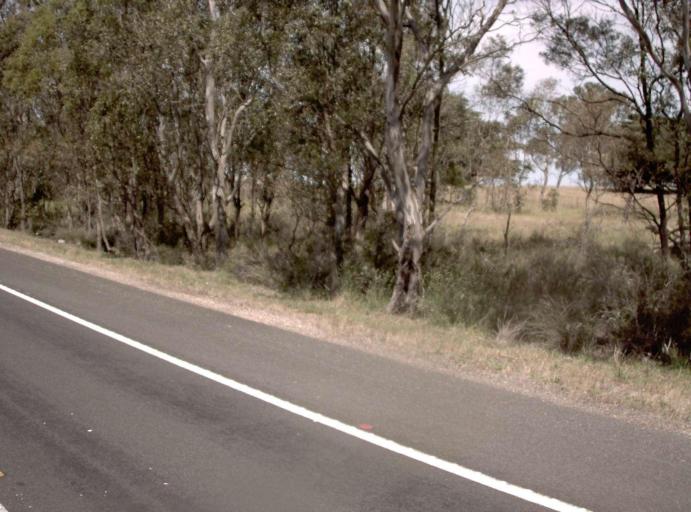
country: AU
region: Victoria
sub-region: East Gippsland
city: Bairnsdale
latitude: -37.8994
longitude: 147.3590
